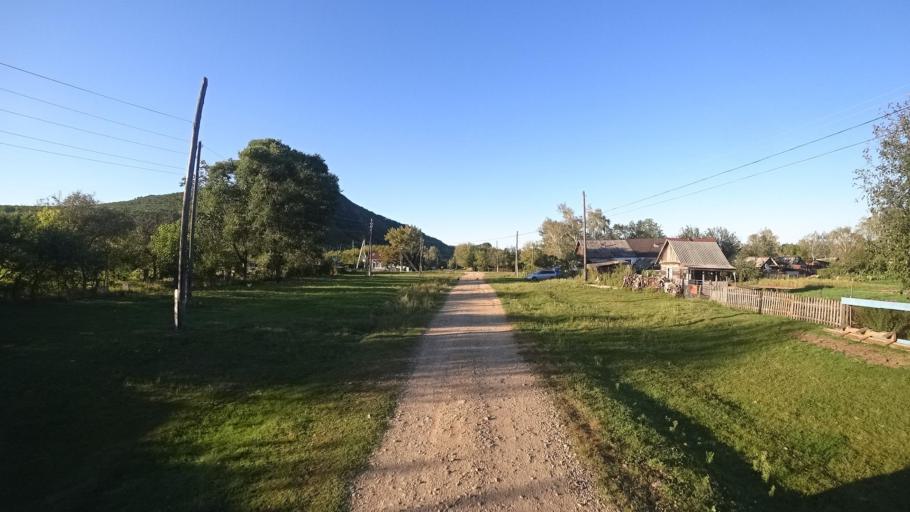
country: RU
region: Primorskiy
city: Kirovskiy
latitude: 44.8312
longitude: 133.5728
